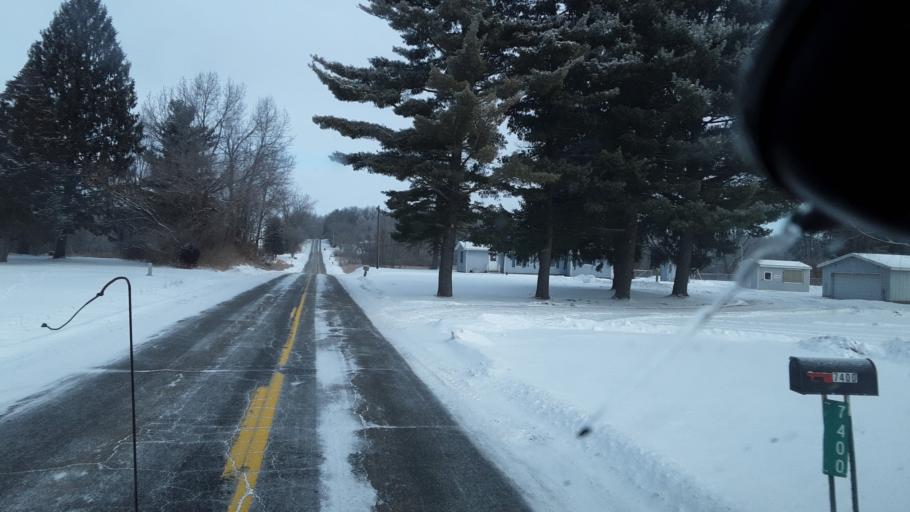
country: US
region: Michigan
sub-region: Jackson County
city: Jackson
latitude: 42.3371
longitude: -84.4827
